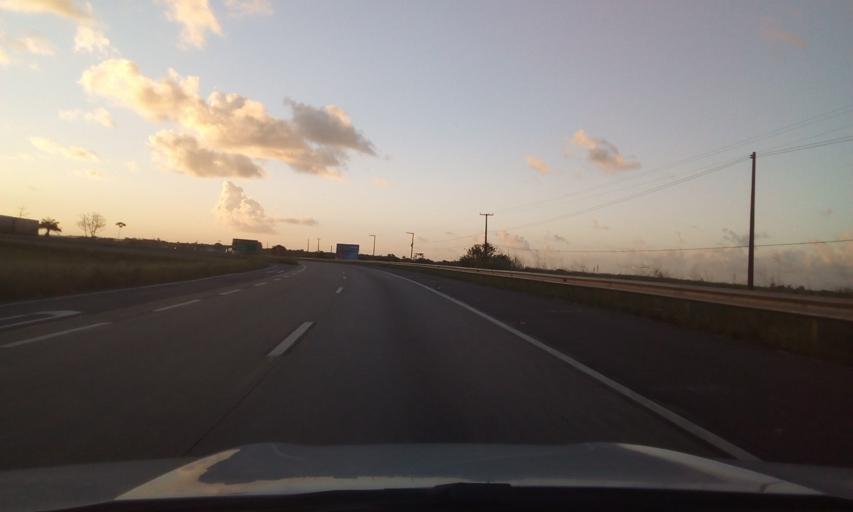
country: BR
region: Pernambuco
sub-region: Goiana
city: Goiana
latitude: -7.6616
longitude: -34.9365
